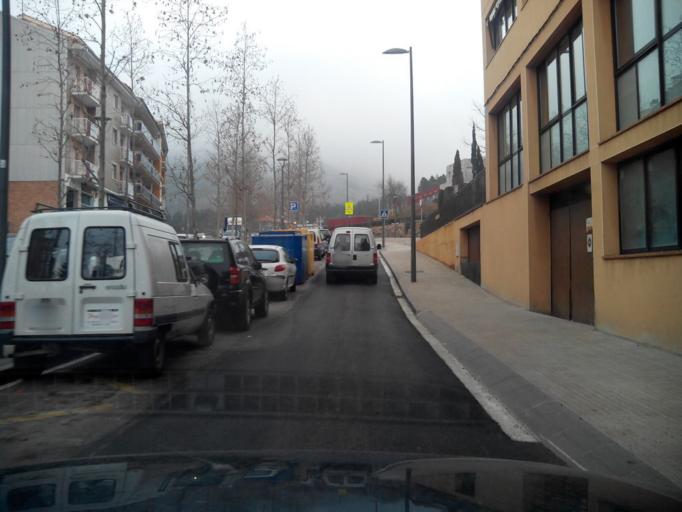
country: ES
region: Catalonia
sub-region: Provincia de Barcelona
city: Berga
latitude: 42.1029
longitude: 1.8576
